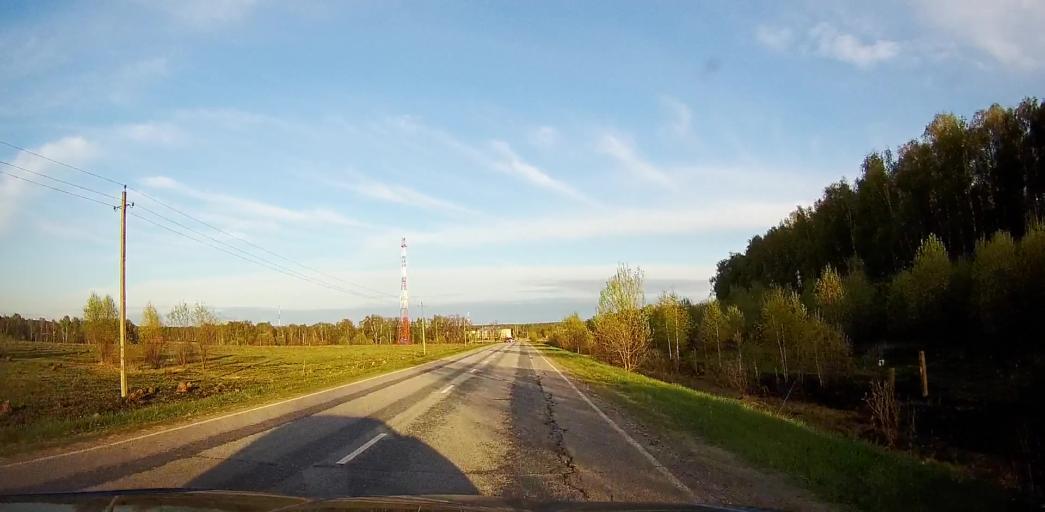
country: RU
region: Moskovskaya
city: Meshcherino
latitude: 55.2357
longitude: 38.3529
